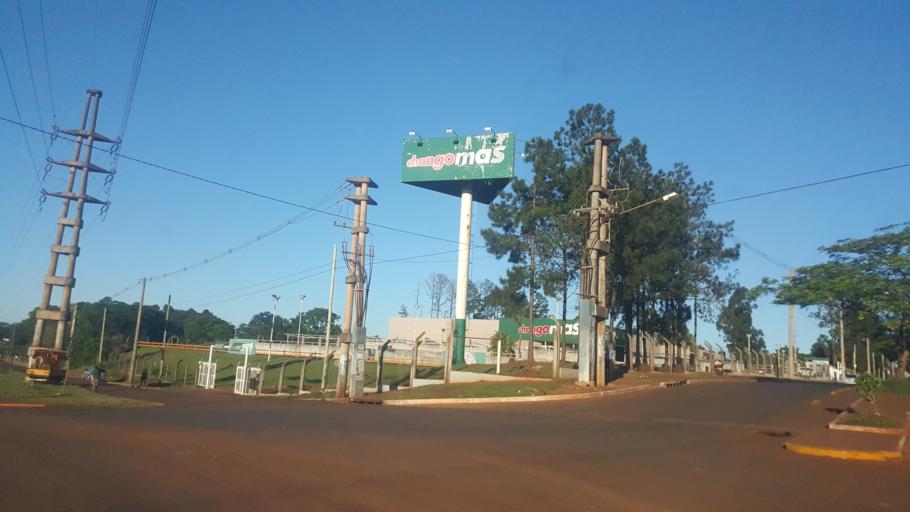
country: AR
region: Misiones
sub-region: Departamento de Capital
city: Posadas
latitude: -27.4256
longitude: -55.9341
